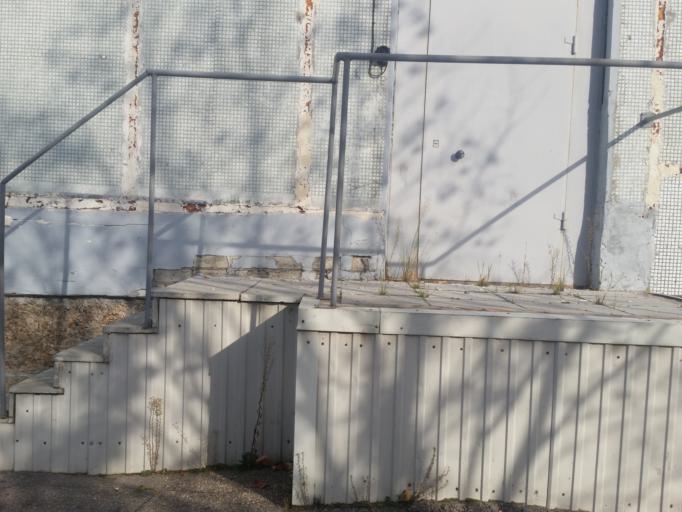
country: RU
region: Ulyanovsk
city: Dimitrovgrad
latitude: 54.2434
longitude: 49.5986
